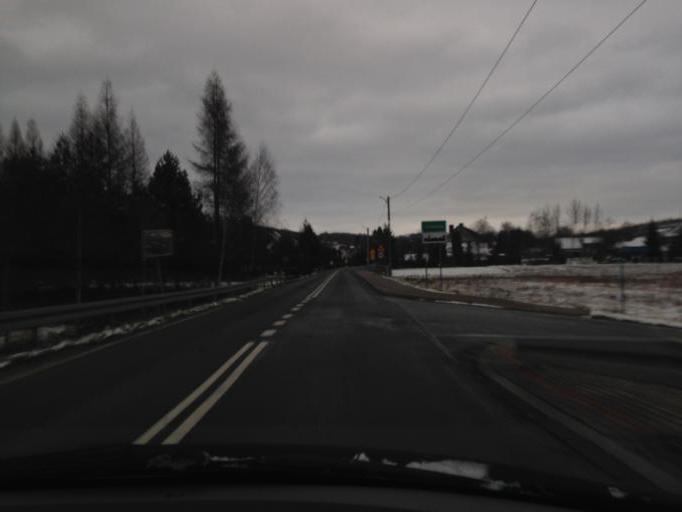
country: PL
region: Lesser Poland Voivodeship
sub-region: Powiat tarnowski
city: Gromnik
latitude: 49.8397
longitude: 20.9817
